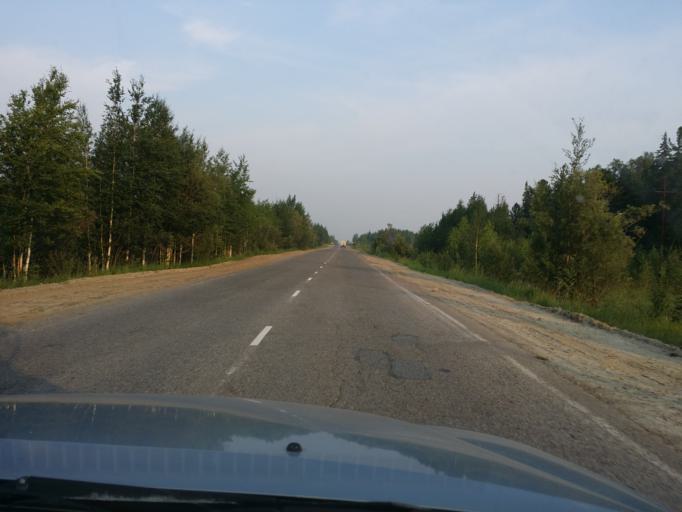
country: RU
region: Khanty-Mansiyskiy Avtonomnyy Okrug
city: Nizhnevartovsk
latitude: 61.2053
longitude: 76.5305
